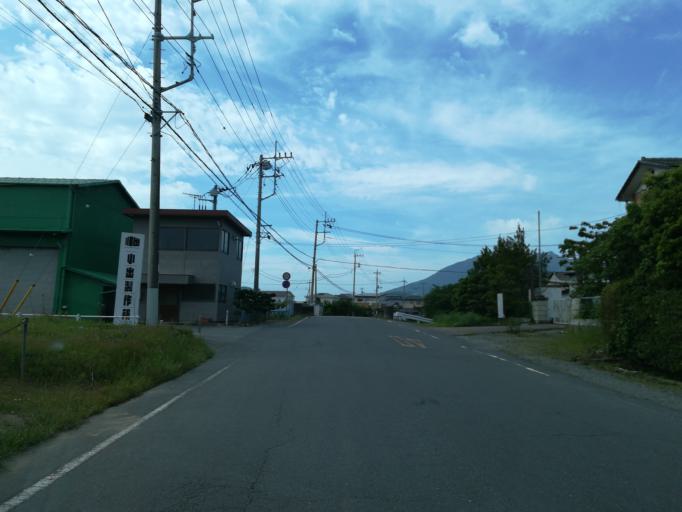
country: JP
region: Ibaraki
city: Tsukuba
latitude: 36.1619
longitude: 140.1059
